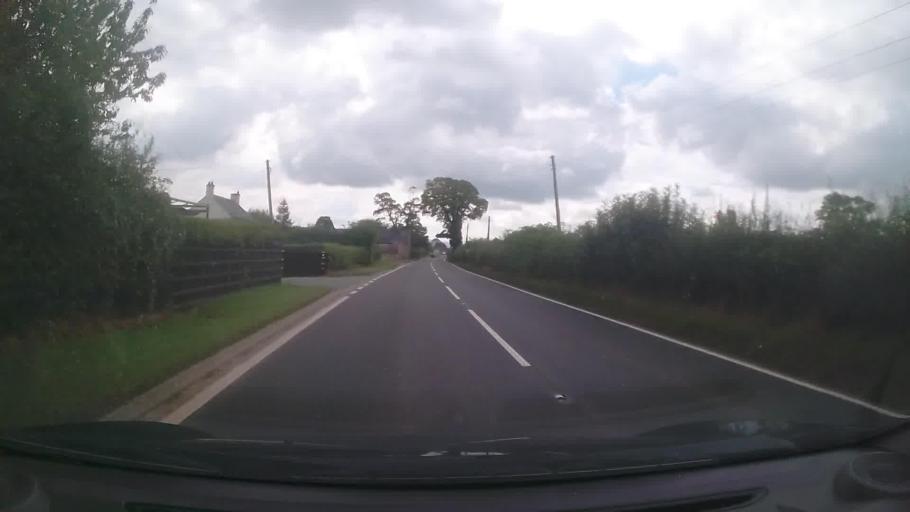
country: GB
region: England
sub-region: Shropshire
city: Pant
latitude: 52.7709
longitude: -3.0852
